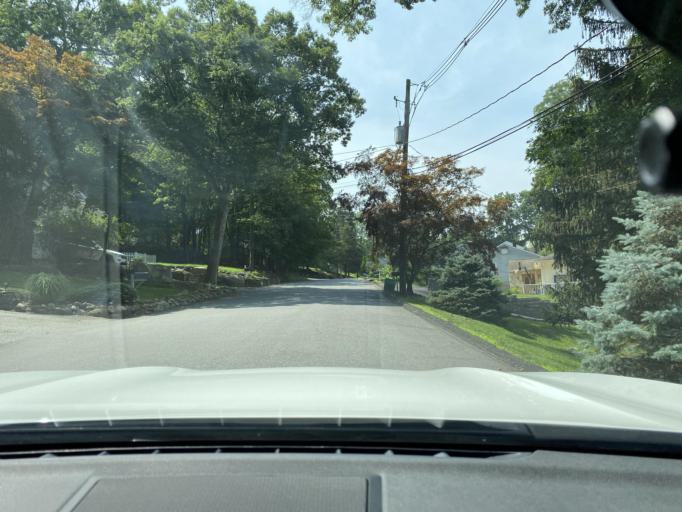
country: US
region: New Jersey
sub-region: Bergen County
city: Franklin Lakes
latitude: 41.0398
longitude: -74.2290
